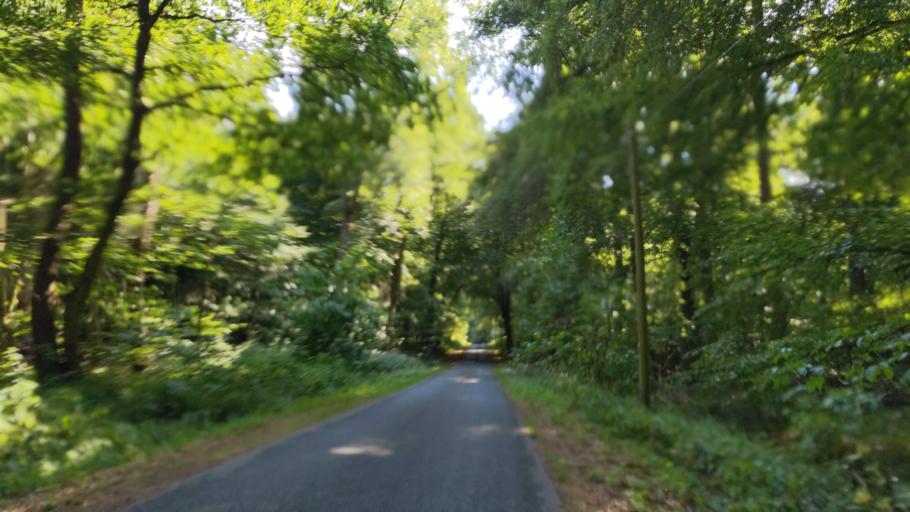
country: DE
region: Schleswig-Holstein
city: Romnitz
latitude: 53.7351
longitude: 10.7692
